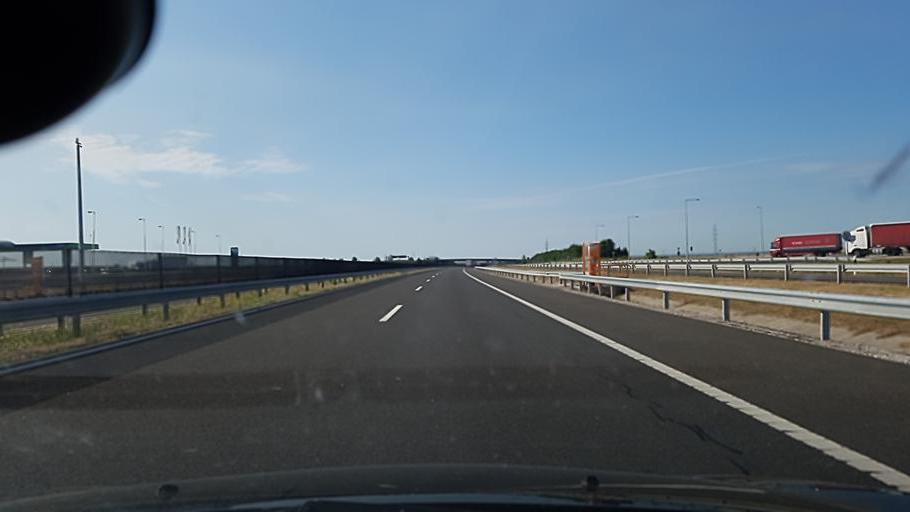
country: HU
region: Fejer
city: dunaujvaros
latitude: 46.9644
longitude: 18.8914
